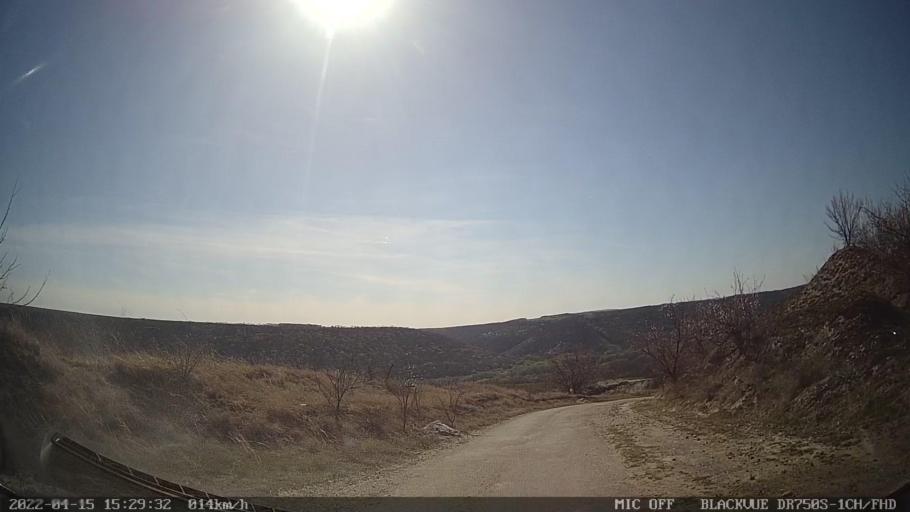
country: MD
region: Raionul Ocnita
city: Otaci
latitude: 48.3553
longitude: 27.9252
